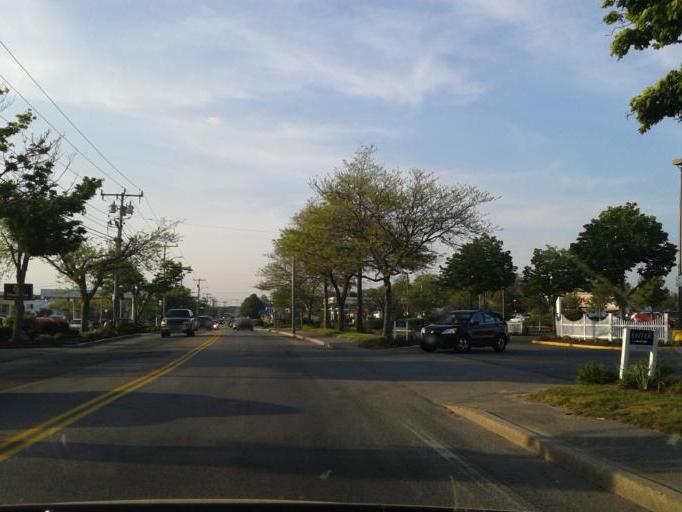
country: US
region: Massachusetts
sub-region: Barnstable County
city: Teaticket
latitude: 41.5559
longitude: -70.5997
